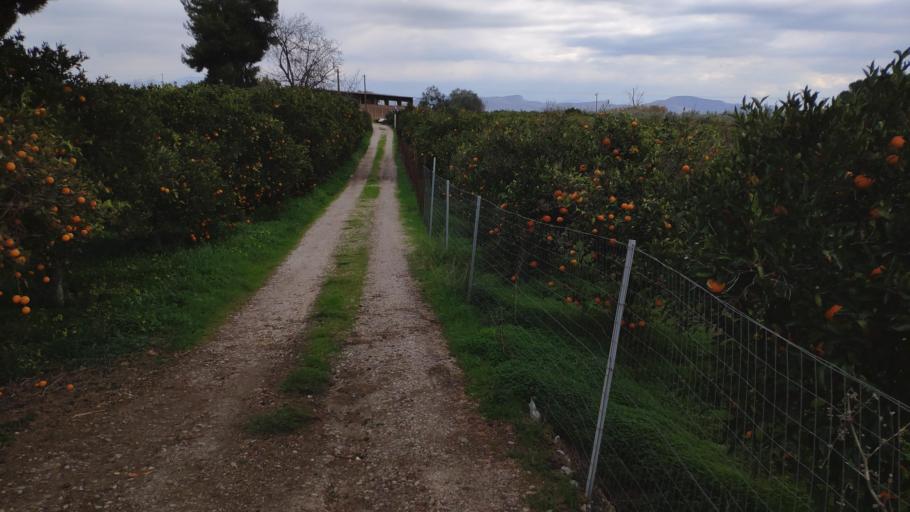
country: GR
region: Peloponnese
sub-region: Nomos Argolidos
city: Nea Kios
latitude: 37.5509
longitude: 22.7169
